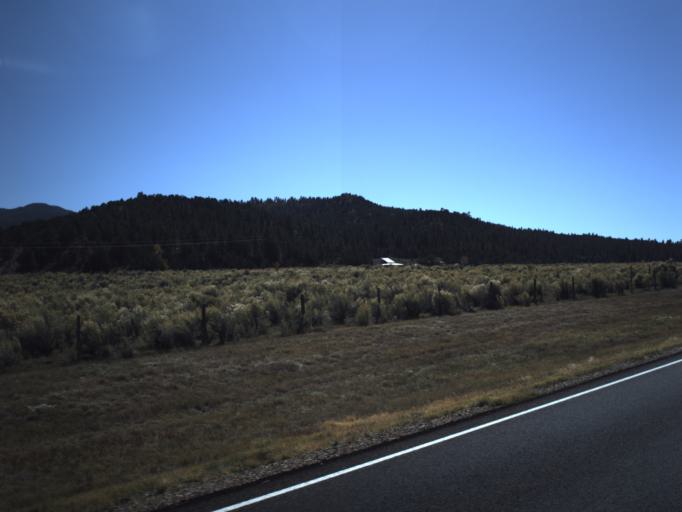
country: US
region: Utah
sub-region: Garfield County
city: Panguitch
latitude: 37.6834
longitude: -111.8124
